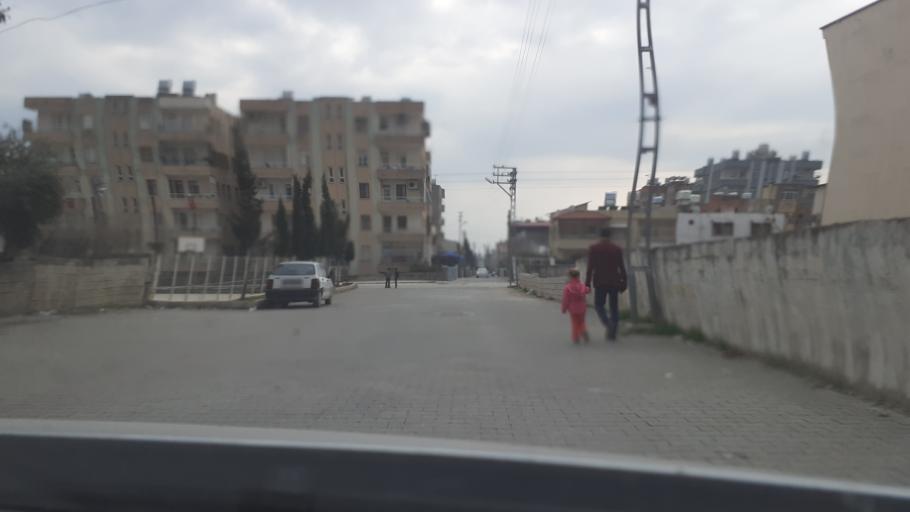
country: TR
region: Hatay
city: Kirikhan
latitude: 36.4948
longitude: 36.3526
